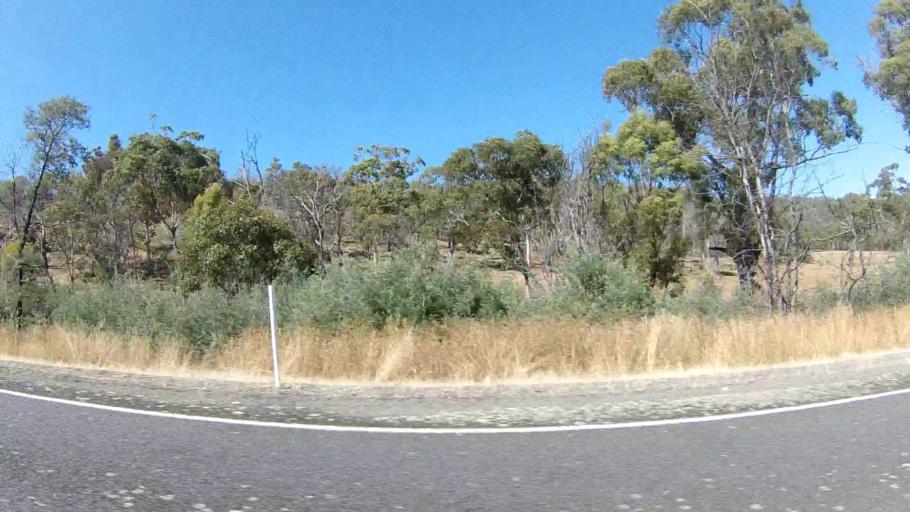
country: AU
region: Tasmania
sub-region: Sorell
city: Sorell
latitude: -42.5896
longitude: 147.7986
